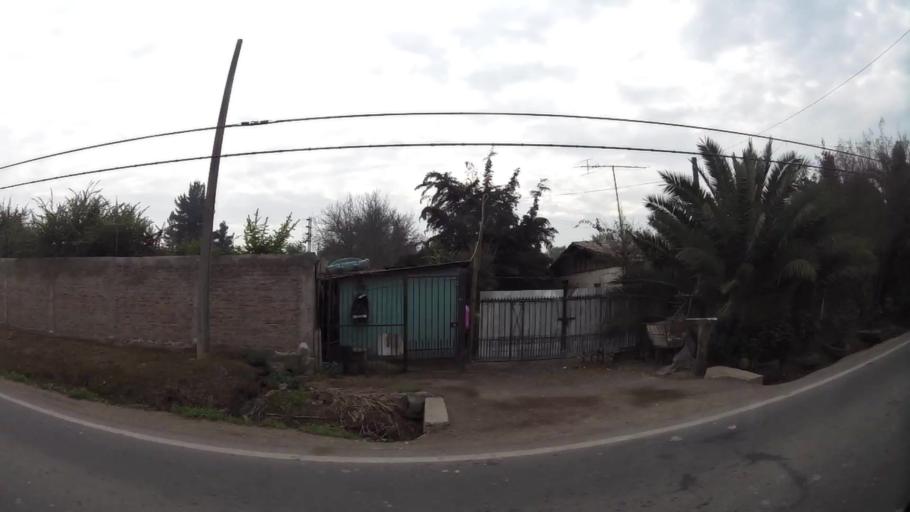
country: CL
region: Santiago Metropolitan
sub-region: Provincia de Chacabuco
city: Chicureo Abajo
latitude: -33.2491
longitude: -70.7212
